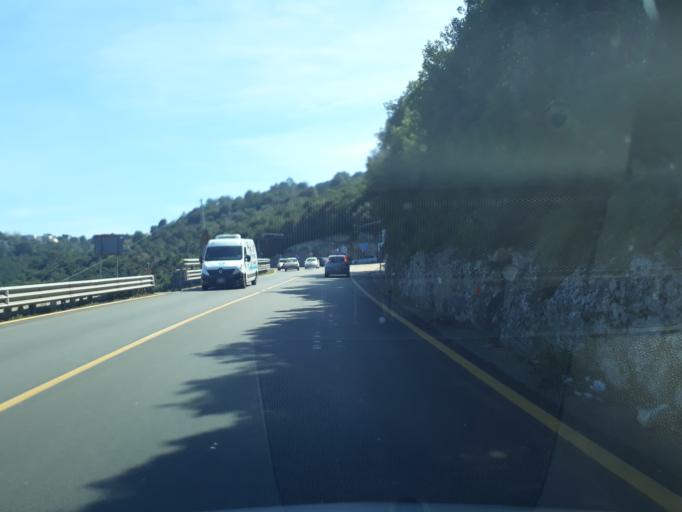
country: IT
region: Apulia
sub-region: Provincia di Brindisi
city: Lamie di Olimpie-Selva
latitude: 40.8075
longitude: 17.3466
